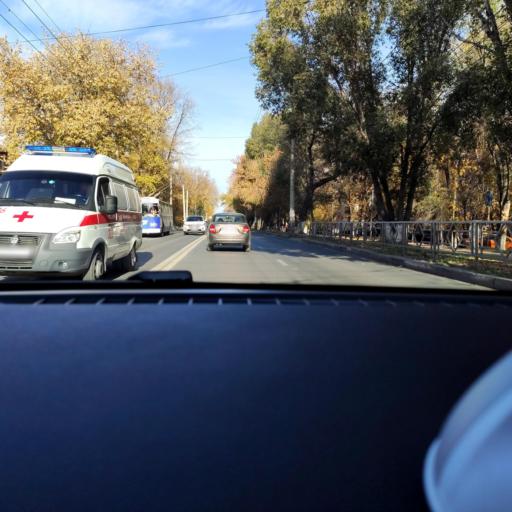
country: RU
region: Samara
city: Samara
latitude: 53.2342
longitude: 50.2439
